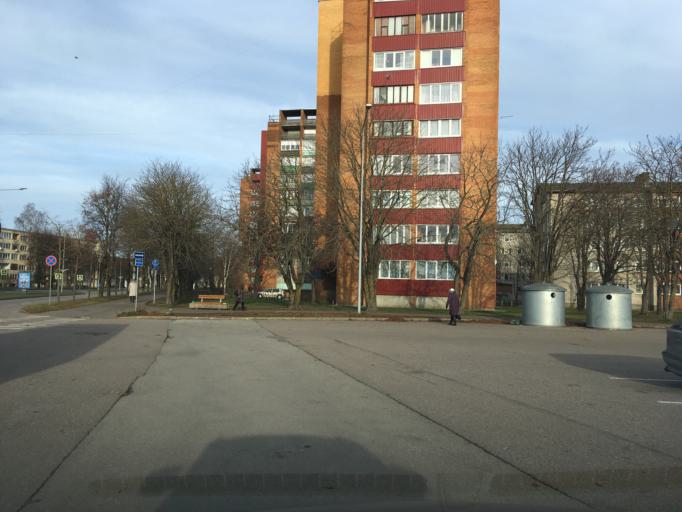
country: EE
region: Ida-Virumaa
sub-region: Narva linn
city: Narva
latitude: 59.3667
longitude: 28.1874
